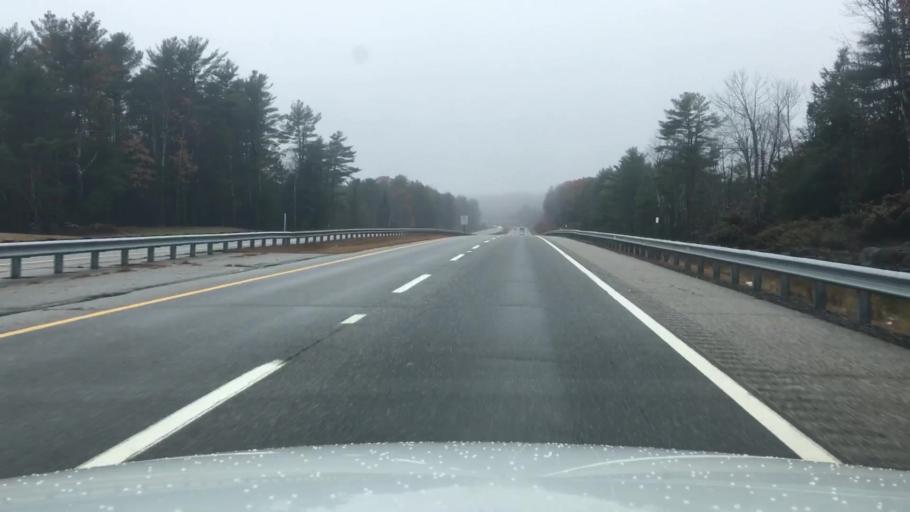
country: US
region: Maine
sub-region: Androscoggin County
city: Sabattus
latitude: 44.1246
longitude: -70.0227
